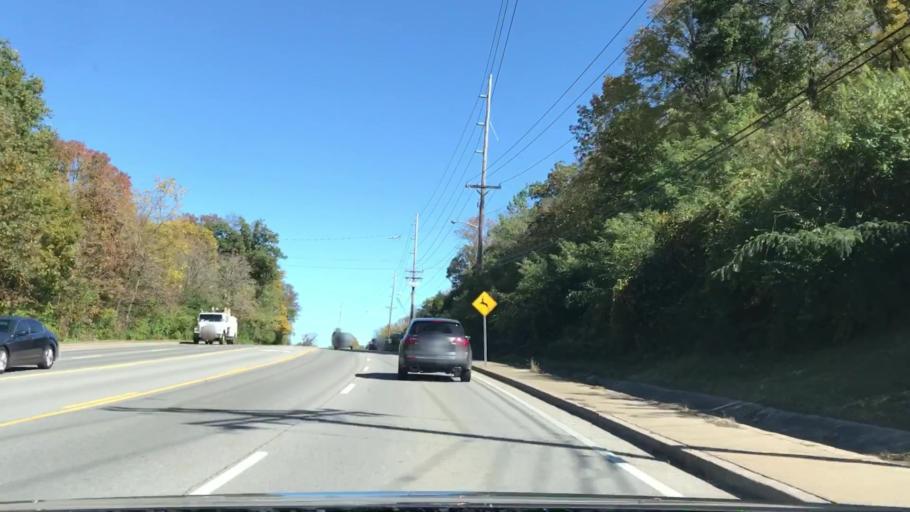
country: US
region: Tennessee
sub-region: Williamson County
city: Brentwood Estates
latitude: 36.0387
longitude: -86.7307
